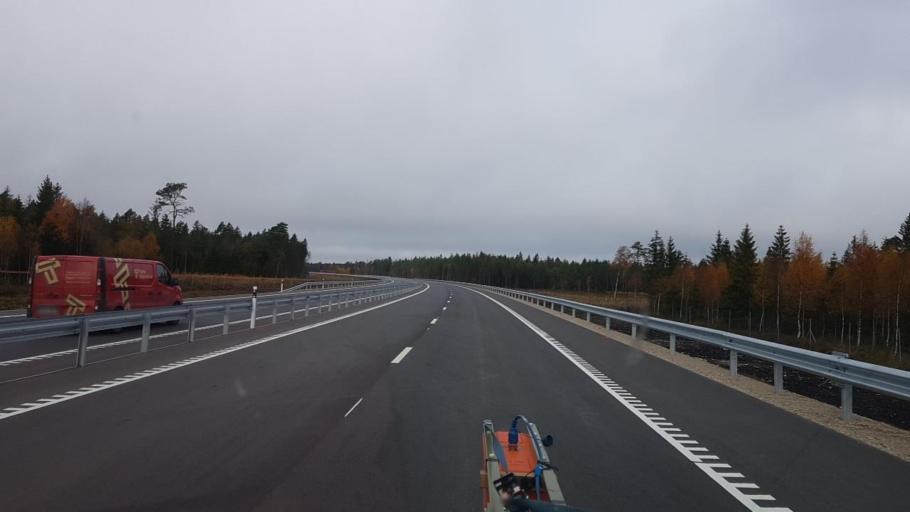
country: EE
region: Jaervamaa
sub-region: Paide linn
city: Paide
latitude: 59.0292
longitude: 25.5339
